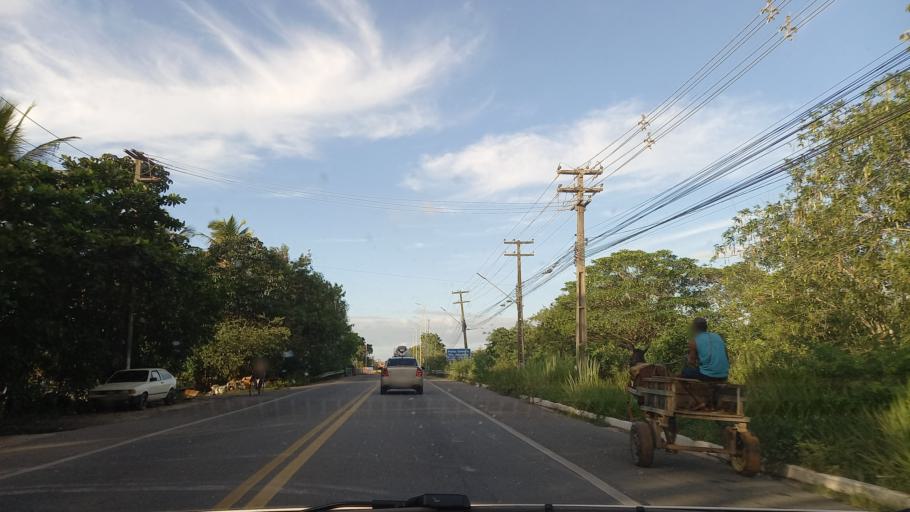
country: BR
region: Pernambuco
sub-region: Jaboatao Dos Guararapes
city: Jaboatao
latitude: -8.2295
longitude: -34.9730
